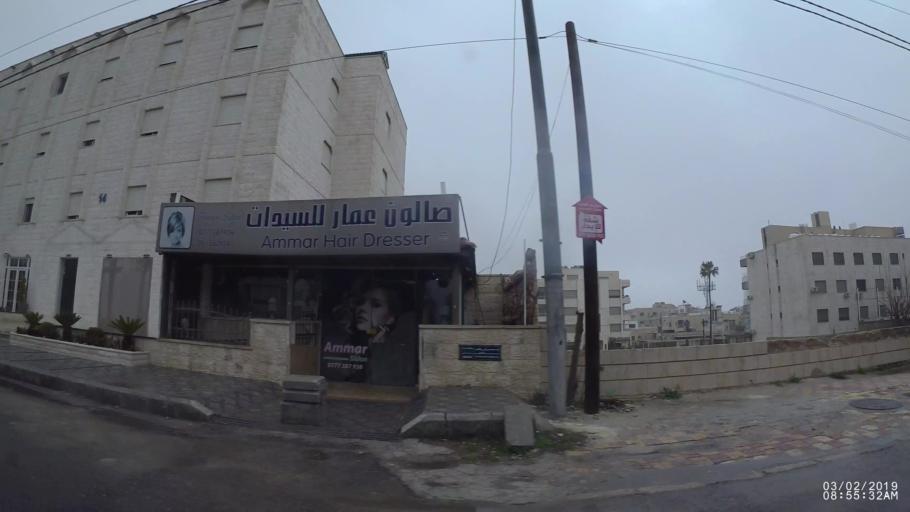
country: JO
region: Amman
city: Wadi as Sir
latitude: 31.9638
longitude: 35.8781
